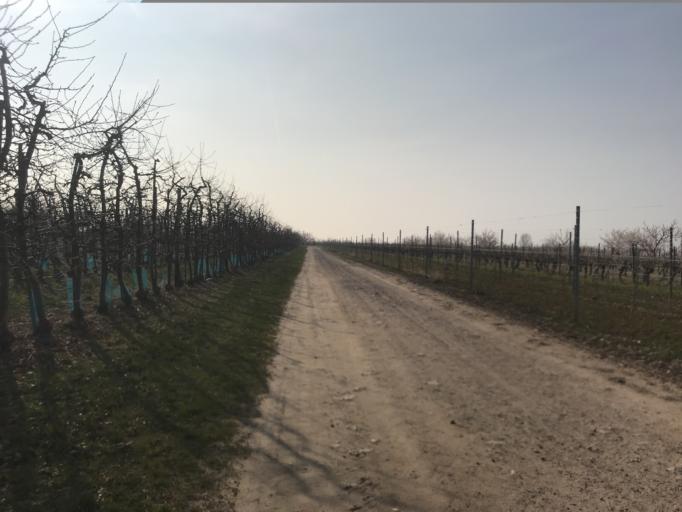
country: DE
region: Rheinland-Pfalz
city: Wackernheim
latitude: 49.9869
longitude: 8.1336
